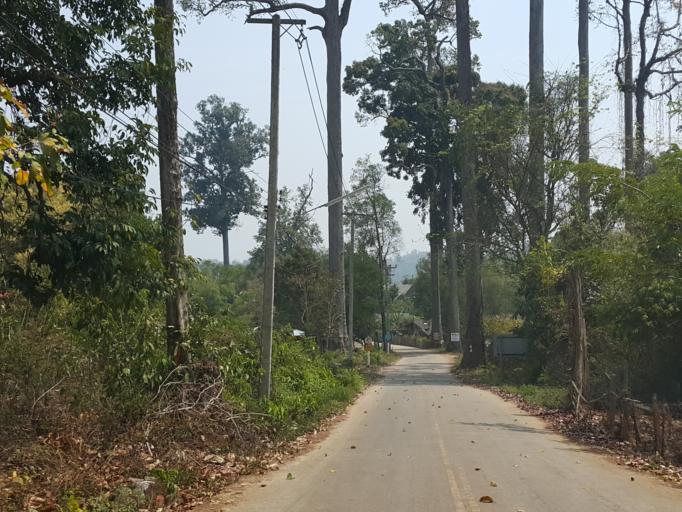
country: TH
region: Lampang
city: Mueang Pan
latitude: 18.8199
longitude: 99.4560
